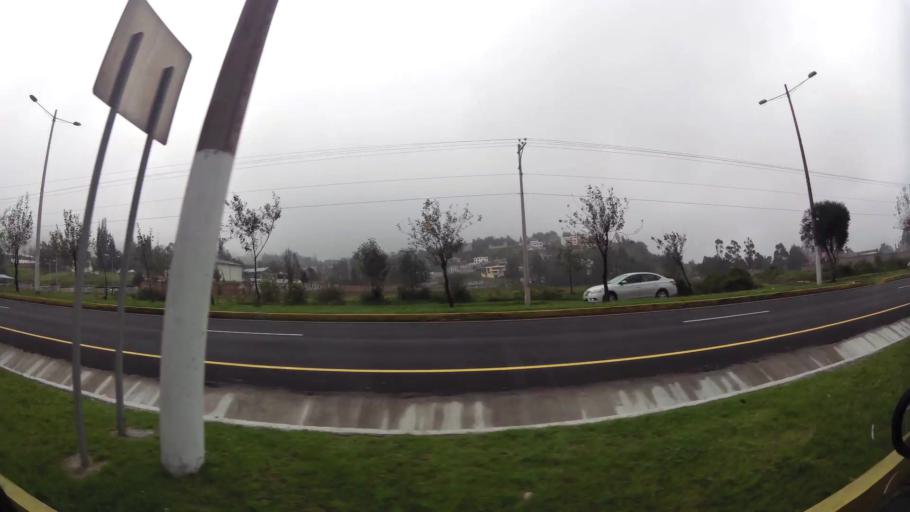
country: EC
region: Pichincha
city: Quito
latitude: -0.2767
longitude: -78.4873
